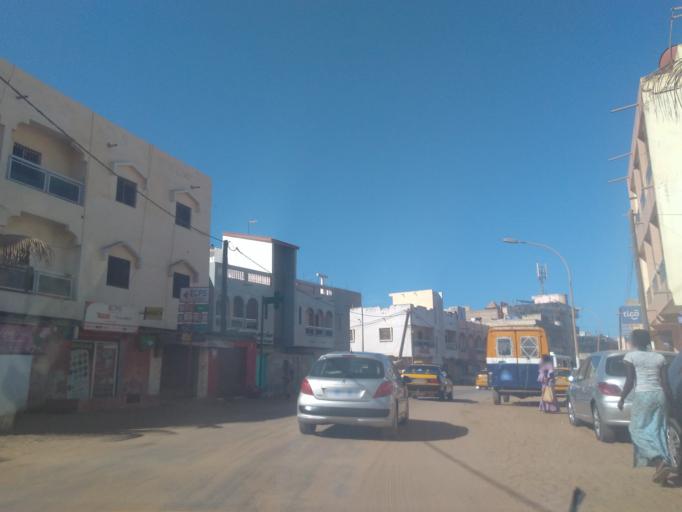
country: SN
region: Dakar
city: Pikine
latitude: 14.7720
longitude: -17.4218
